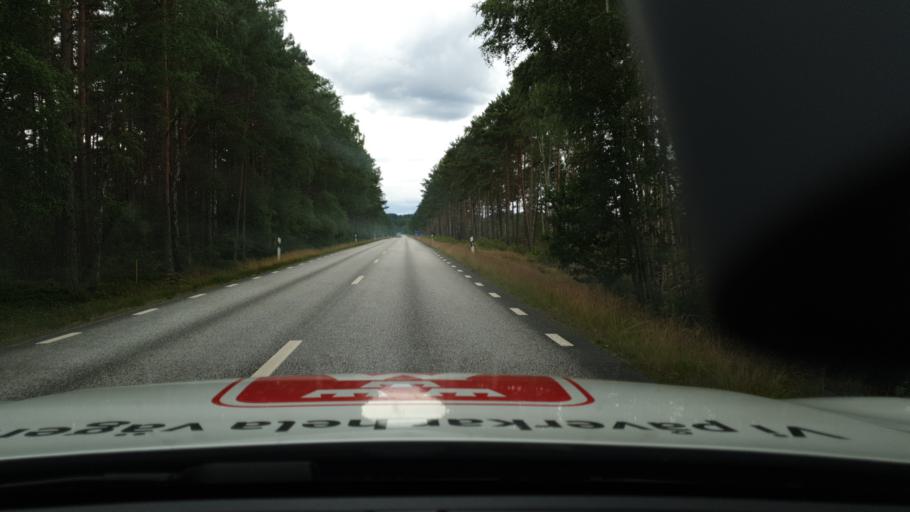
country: SE
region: Joenkoeping
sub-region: Gnosjo Kommun
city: Hillerstorp
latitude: 57.2816
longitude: 13.8167
